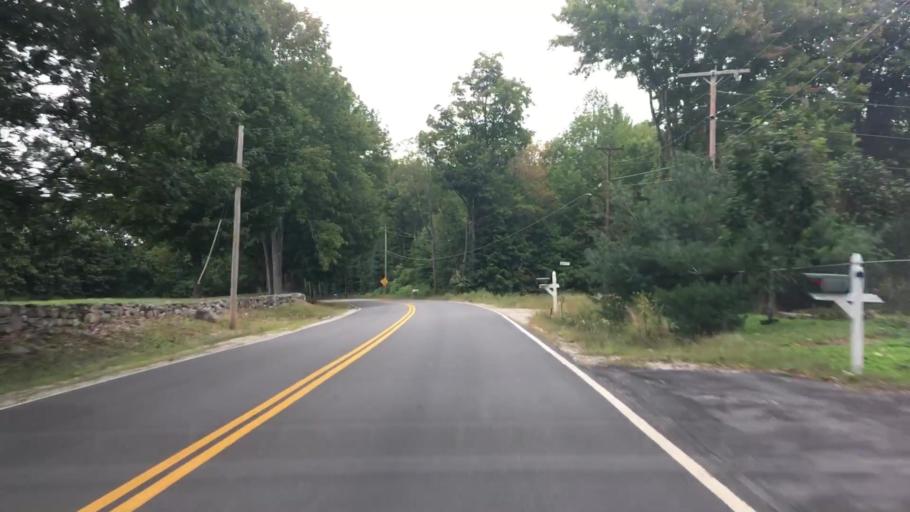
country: US
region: Maine
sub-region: Cumberland County
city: New Gloucester
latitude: 43.9083
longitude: -70.2503
